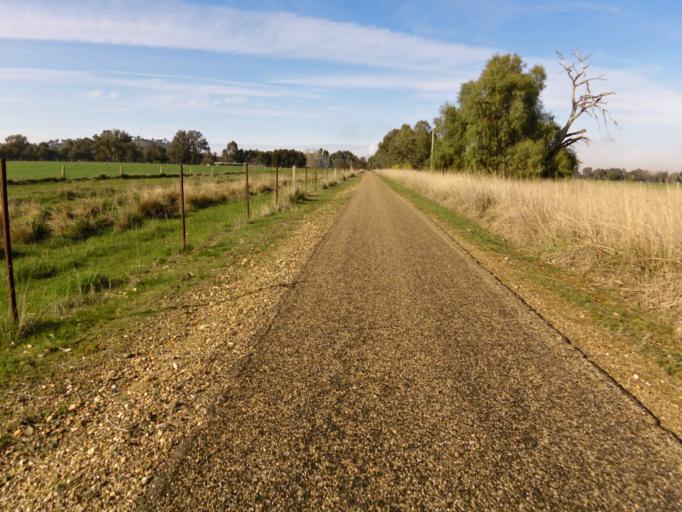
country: AU
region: Victoria
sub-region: Wangaratta
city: Wangaratta
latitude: -36.4254
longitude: 146.5504
